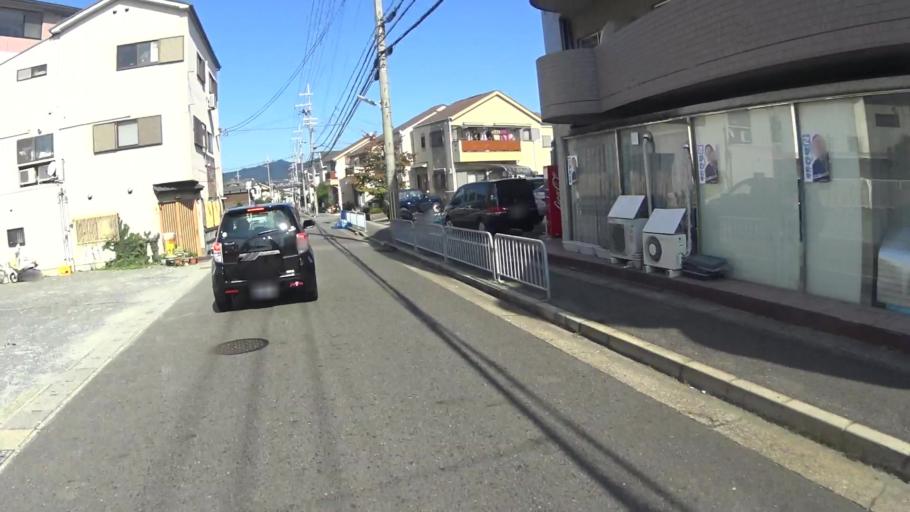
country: JP
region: Kyoto
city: Muko
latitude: 34.9671
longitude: 135.6795
